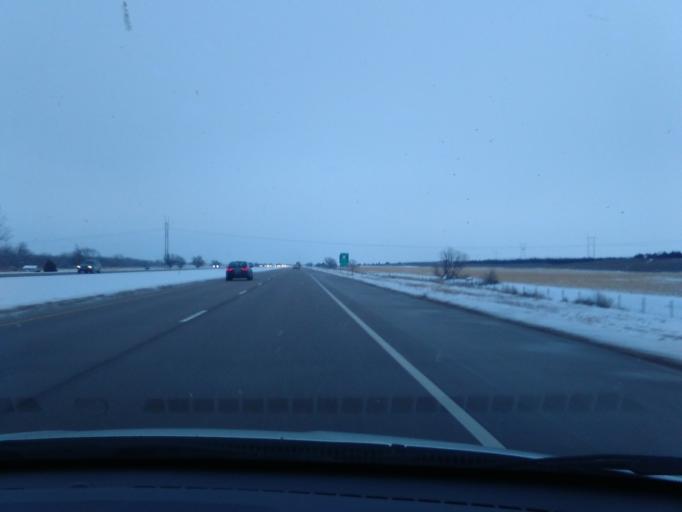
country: US
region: Nebraska
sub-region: Lincoln County
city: Sutherland
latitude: 41.1081
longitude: -101.3816
